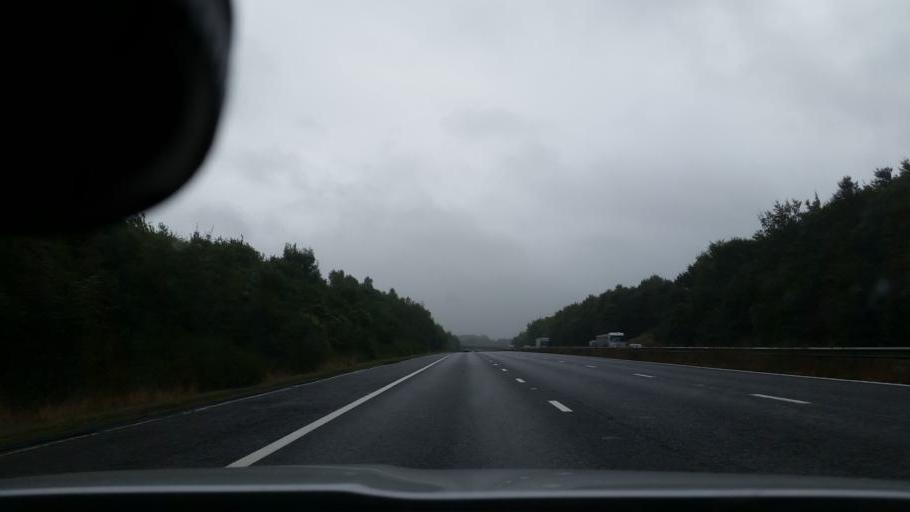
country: GB
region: England
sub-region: Kent
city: Eynsford
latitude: 51.3675
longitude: 0.2591
